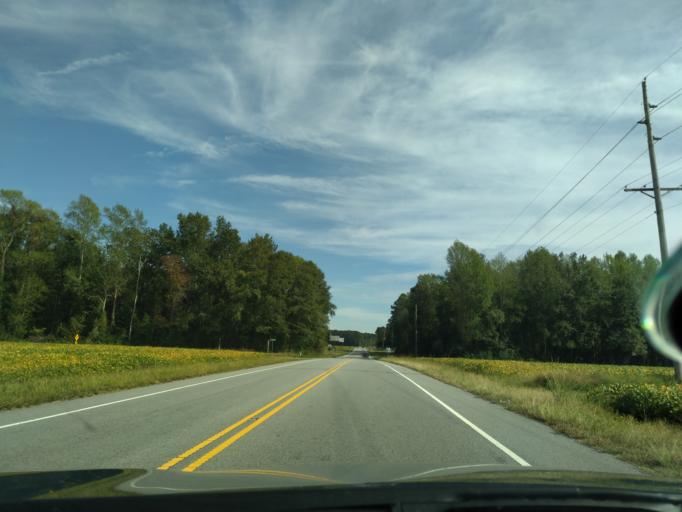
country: US
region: North Carolina
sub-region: Beaufort County
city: River Road
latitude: 35.5242
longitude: -76.9392
